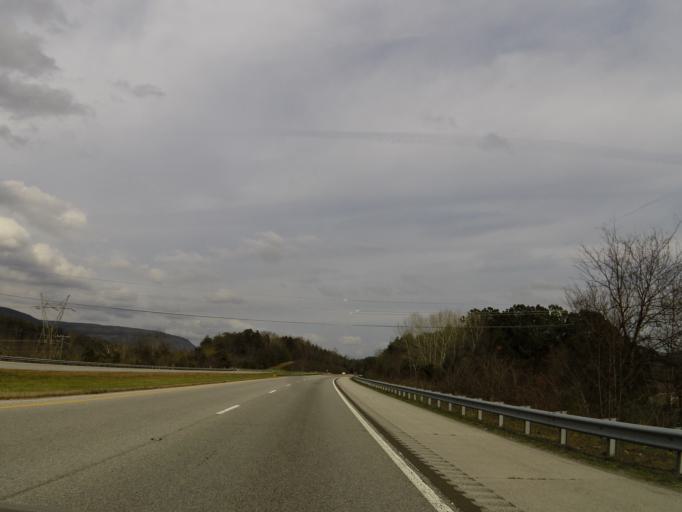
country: US
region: Tennessee
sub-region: Hamilton County
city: Walden
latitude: 35.1761
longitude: -85.2750
